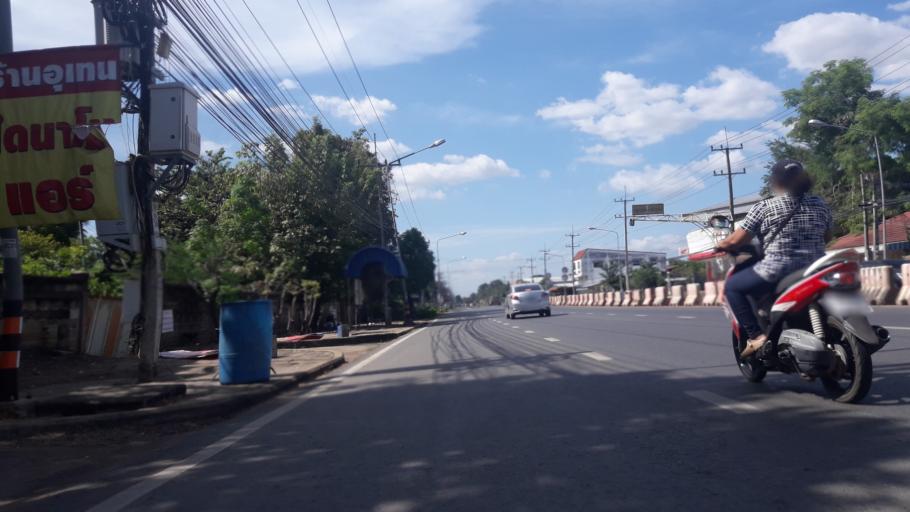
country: TH
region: Phichit
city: Thap Khlo
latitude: 16.1697
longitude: 100.5730
